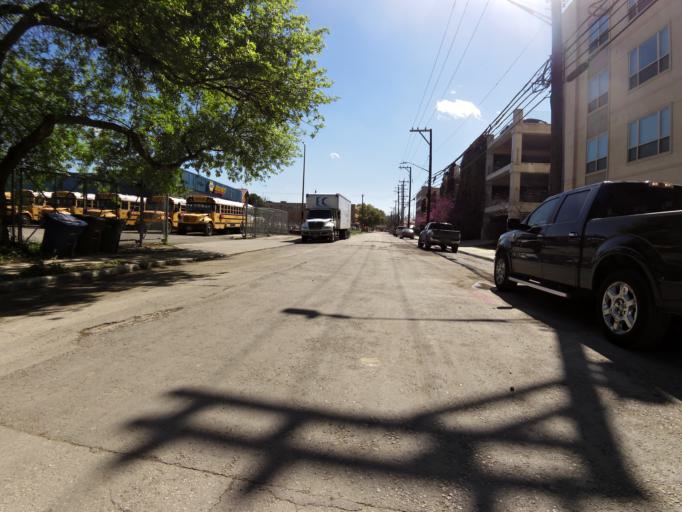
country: US
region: Texas
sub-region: Bexar County
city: San Antonio
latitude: 29.4431
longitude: -98.4757
